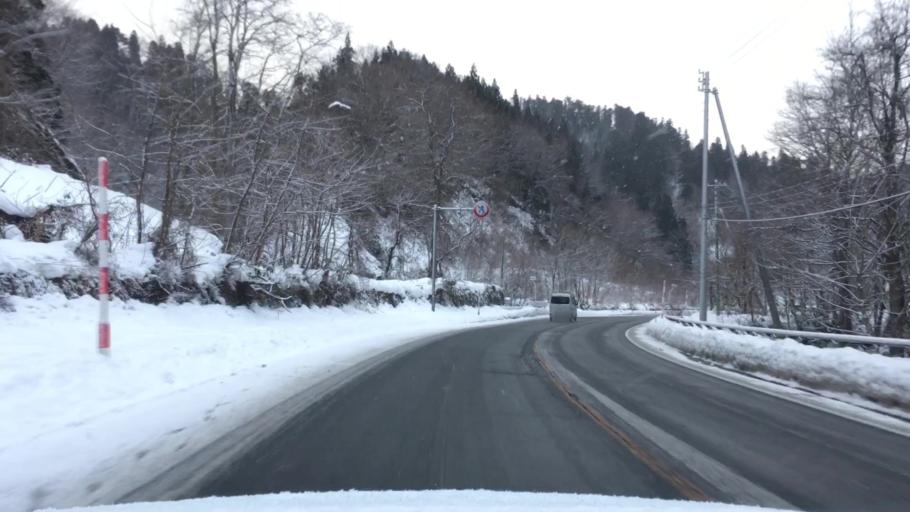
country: JP
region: Akita
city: Odate
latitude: 40.4300
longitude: 140.6371
